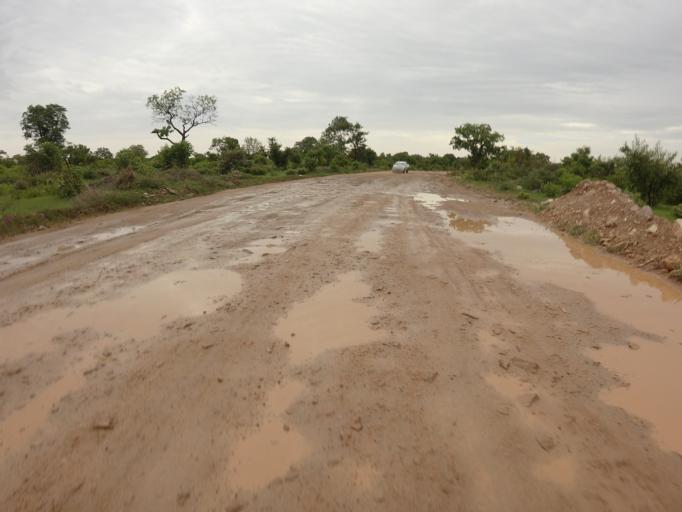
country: GH
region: Upper East
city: Bolgatanga
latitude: 10.8772
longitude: -0.6373
